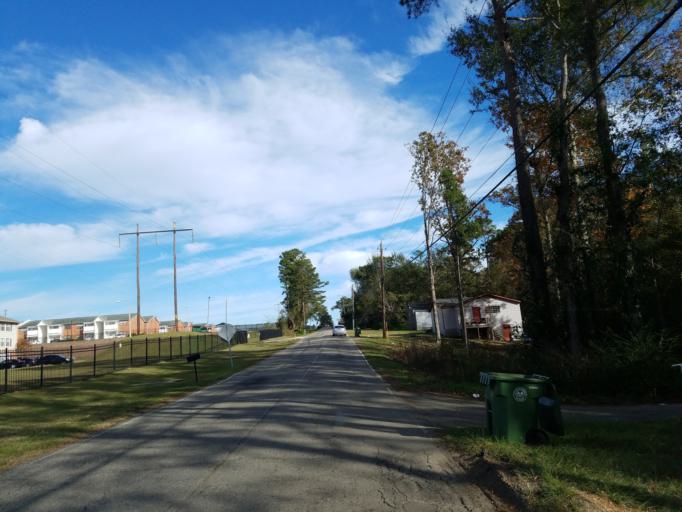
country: US
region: Mississippi
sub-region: Lamar County
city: Arnold Line
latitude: 31.3466
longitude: -89.3408
